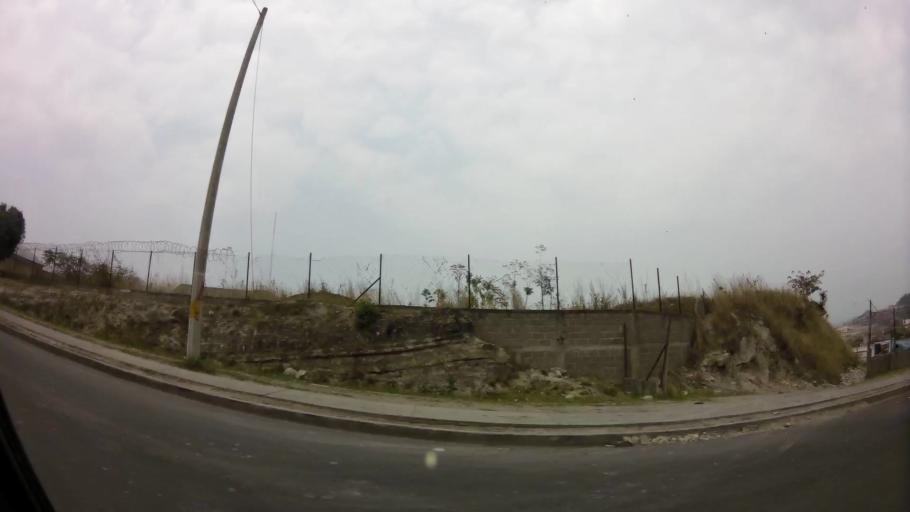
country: HN
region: Francisco Morazan
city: Tegucigalpa
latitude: 14.0563
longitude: -87.2542
